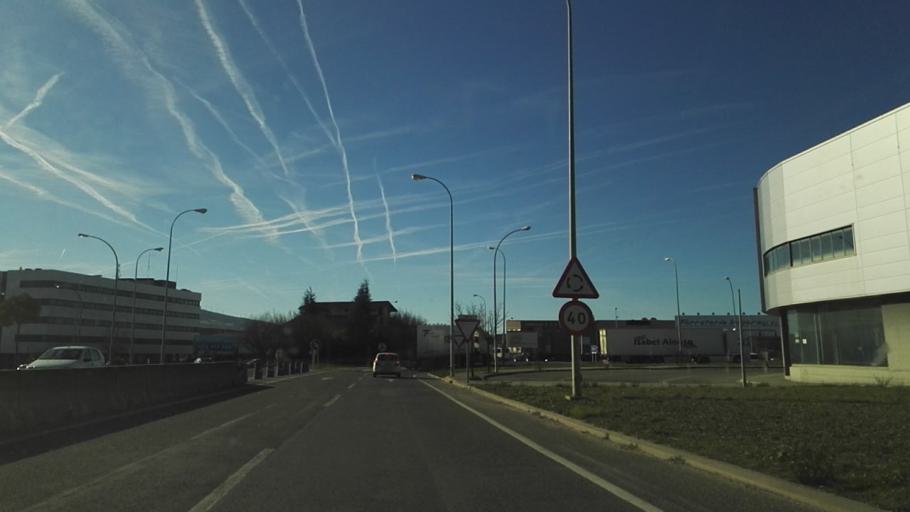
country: ES
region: Navarre
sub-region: Provincia de Navarra
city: Segundo Ensanche
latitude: 42.7749
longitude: -1.6339
